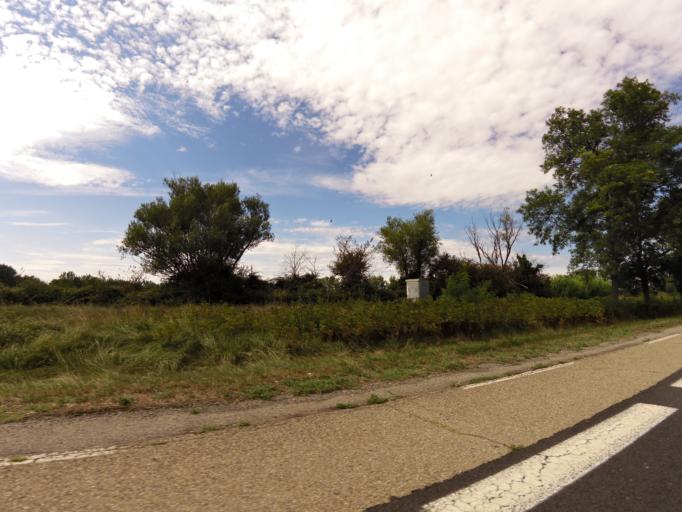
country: FR
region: Languedoc-Roussillon
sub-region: Departement de l'Herault
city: Marsillargues
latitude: 43.6443
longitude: 4.1962
